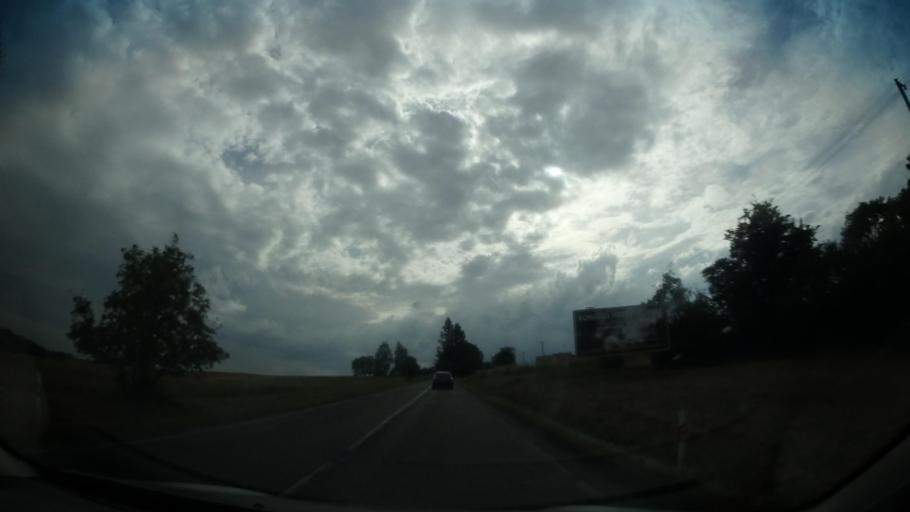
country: CZ
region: Pardubicky
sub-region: Okres Chrudim
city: Sec
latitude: 49.8506
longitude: 15.6701
